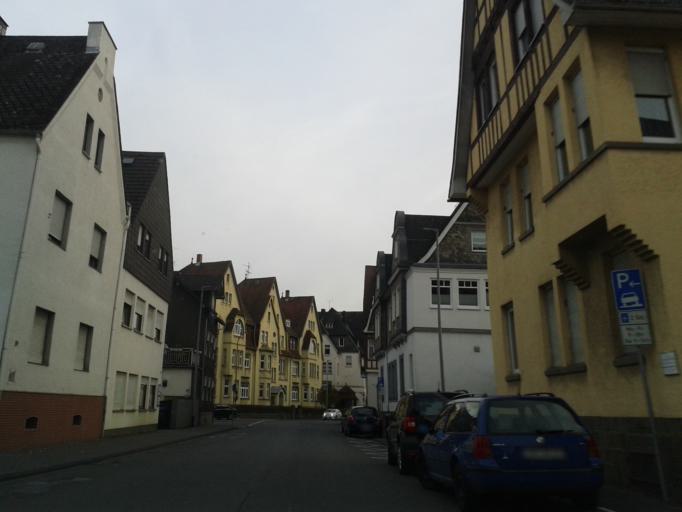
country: DE
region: Hesse
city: Herborn
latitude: 50.6834
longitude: 8.3073
